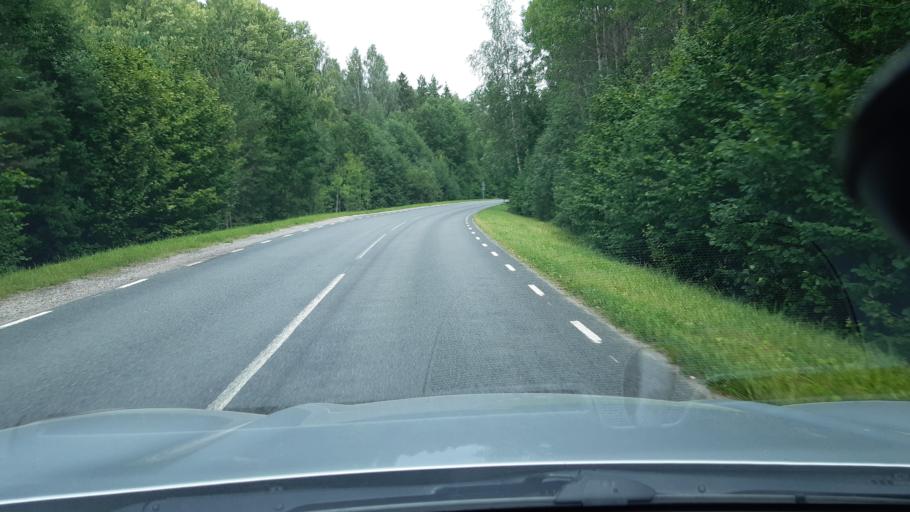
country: EE
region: Raplamaa
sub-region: Maerjamaa vald
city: Marjamaa
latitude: 59.0427
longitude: 24.5116
